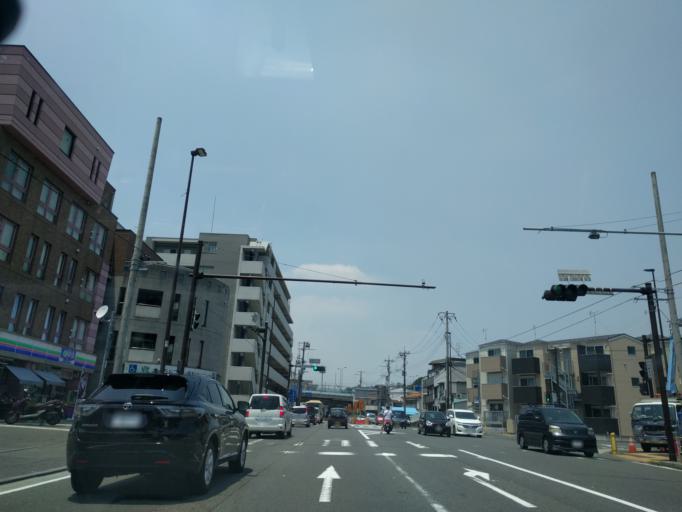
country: JP
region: Kanagawa
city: Yokohama
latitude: 35.4718
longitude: 139.5759
